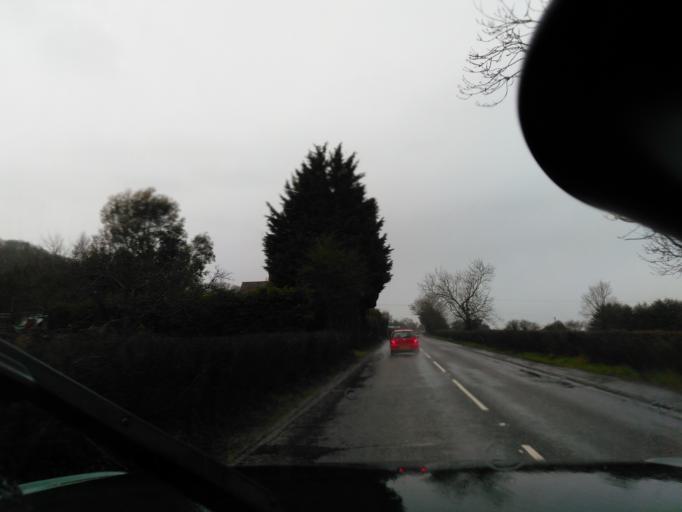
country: GB
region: England
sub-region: Somerset
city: Wells
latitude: 51.1505
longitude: -2.6311
